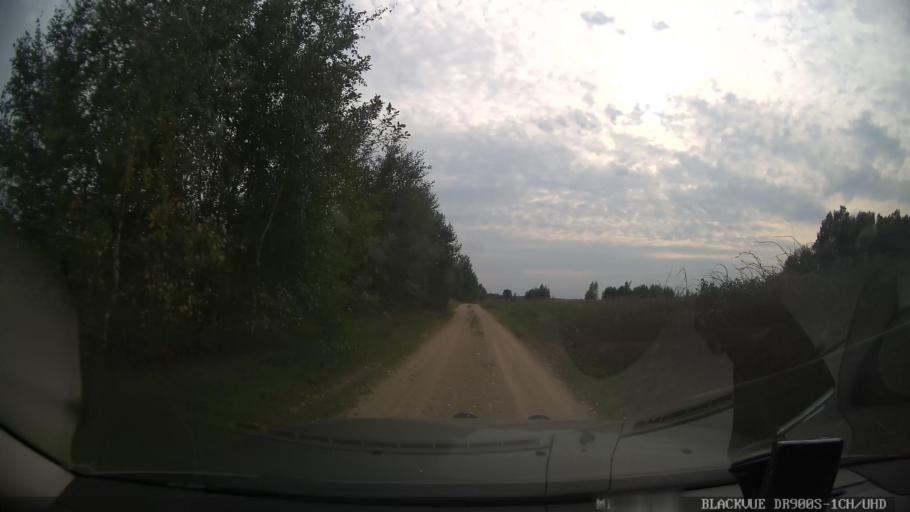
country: BY
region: Grodnenskaya
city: Ashmyany
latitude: 54.5354
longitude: 25.6737
